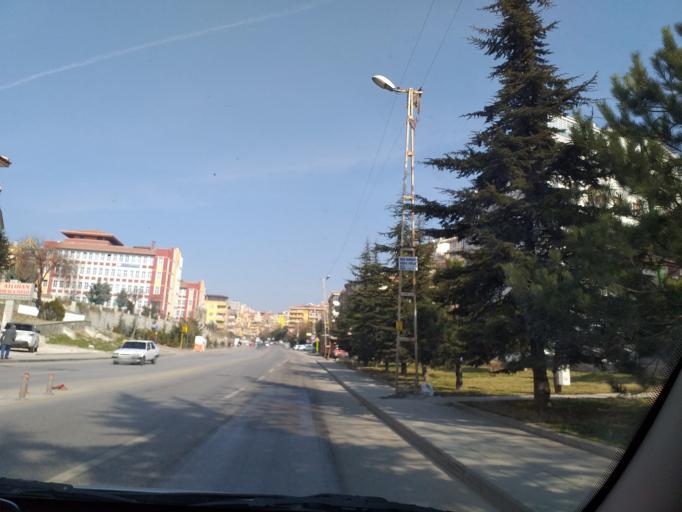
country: TR
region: Ankara
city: Ankara
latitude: 39.9923
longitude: 32.8567
